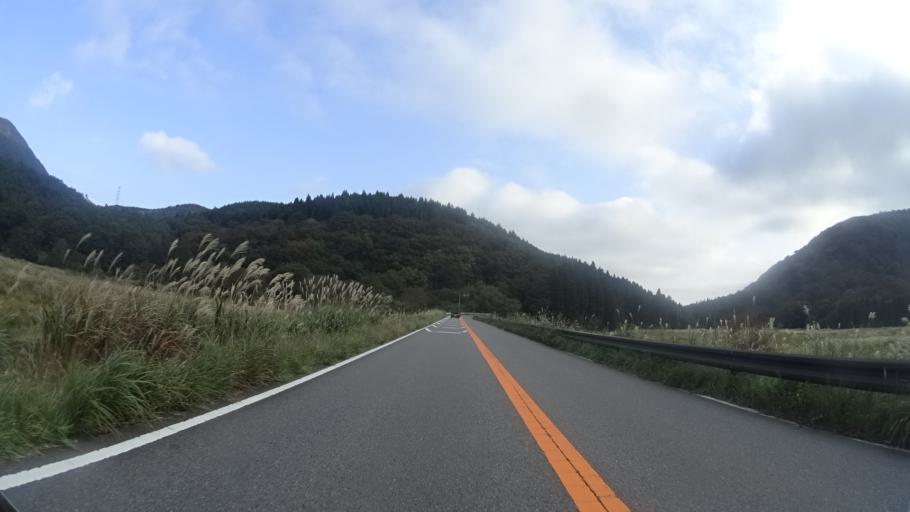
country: JP
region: Oita
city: Beppu
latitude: 33.2744
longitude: 131.4153
